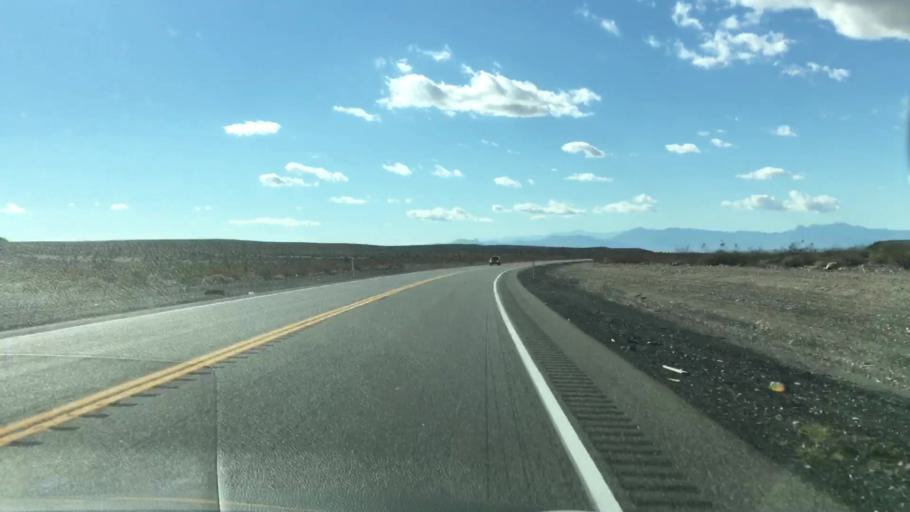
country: US
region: Nevada
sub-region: Nye County
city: Pahrump
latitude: 36.5633
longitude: -116.0875
